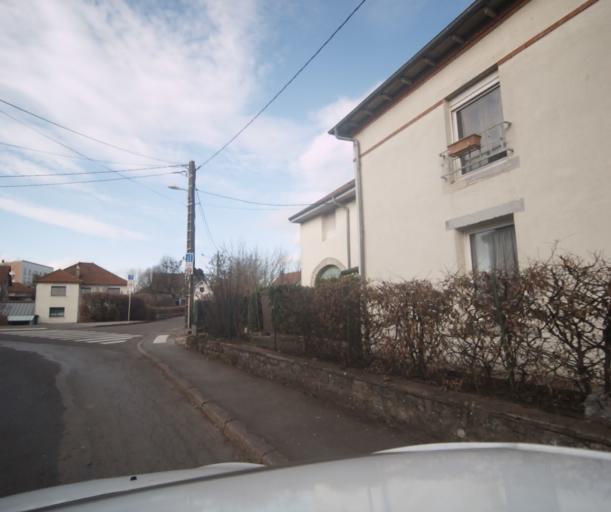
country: FR
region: Franche-Comte
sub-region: Departement du Doubs
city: Besancon
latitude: 47.2597
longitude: 6.0287
